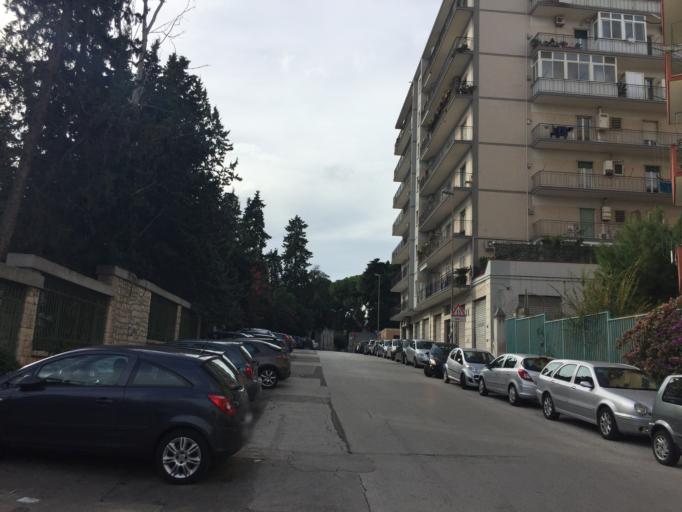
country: IT
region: Apulia
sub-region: Provincia di Bari
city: Bari
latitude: 41.1123
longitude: 16.8810
